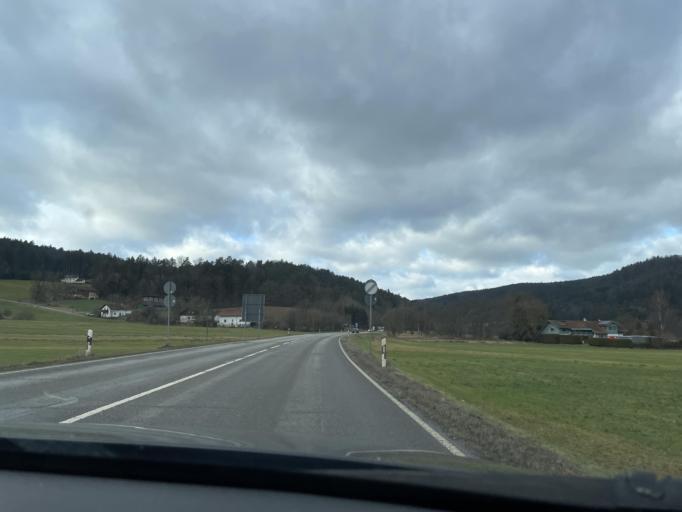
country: DE
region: Bavaria
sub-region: Upper Palatinate
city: Blaibach
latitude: 49.1595
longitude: 12.8041
